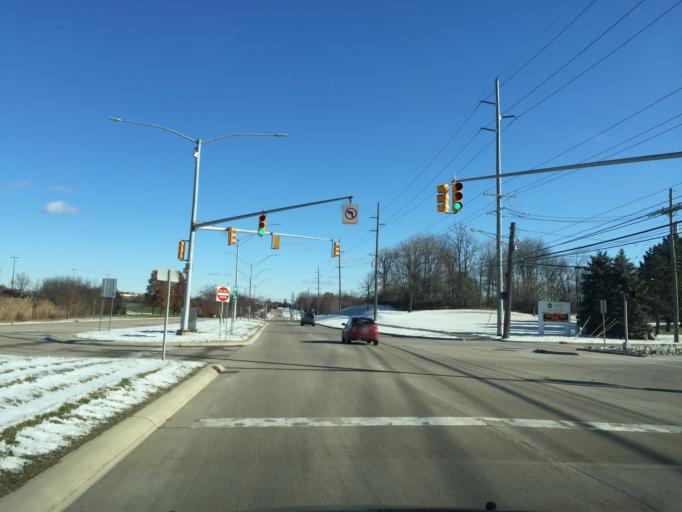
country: US
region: Michigan
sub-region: Oakland County
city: Auburn Hills
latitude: 42.6494
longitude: -83.2298
